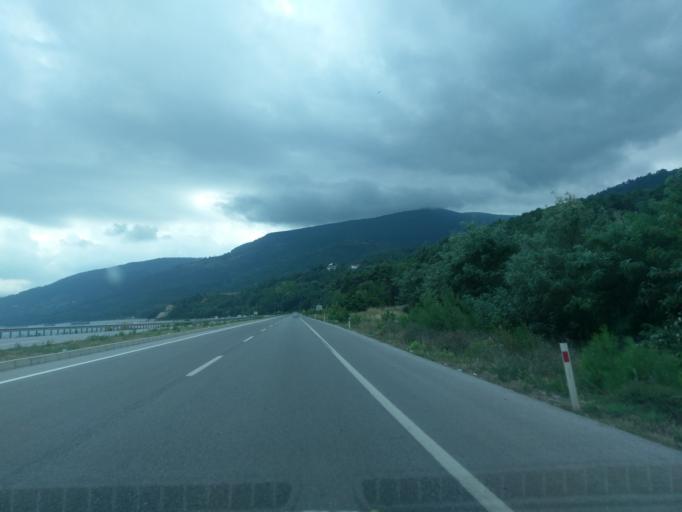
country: TR
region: Sinop
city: Gerze
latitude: 41.7792
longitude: 35.2023
